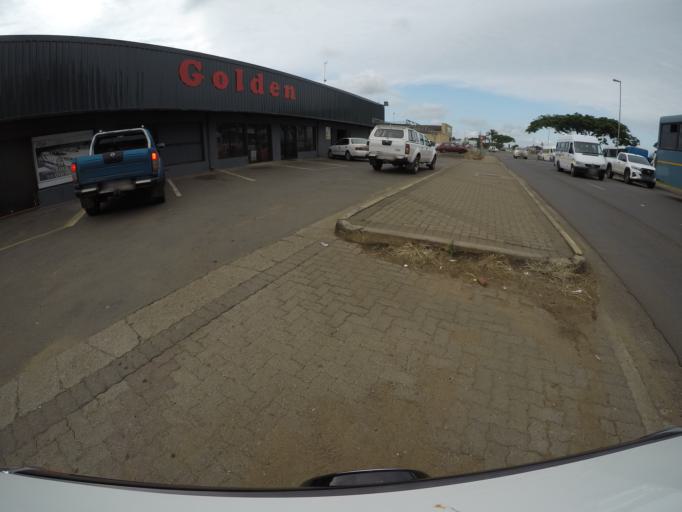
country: ZA
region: KwaZulu-Natal
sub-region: uThungulu District Municipality
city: Empangeni
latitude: -28.7770
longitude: 31.9003
